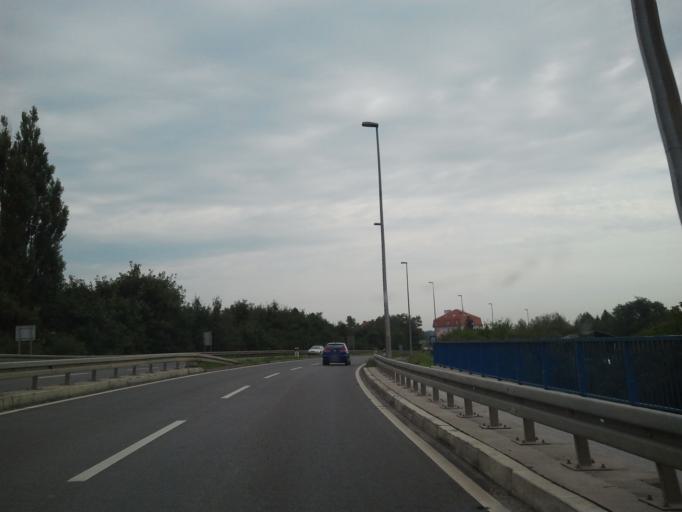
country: HR
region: Karlovacka
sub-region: Grad Karlovac
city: Karlovac
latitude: 45.5094
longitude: 15.5440
